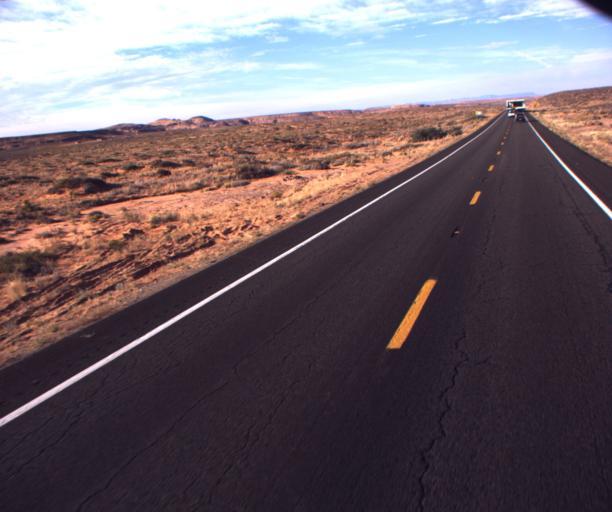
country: US
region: Arizona
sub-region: Apache County
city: Many Farms
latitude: 36.9333
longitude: -109.5667
